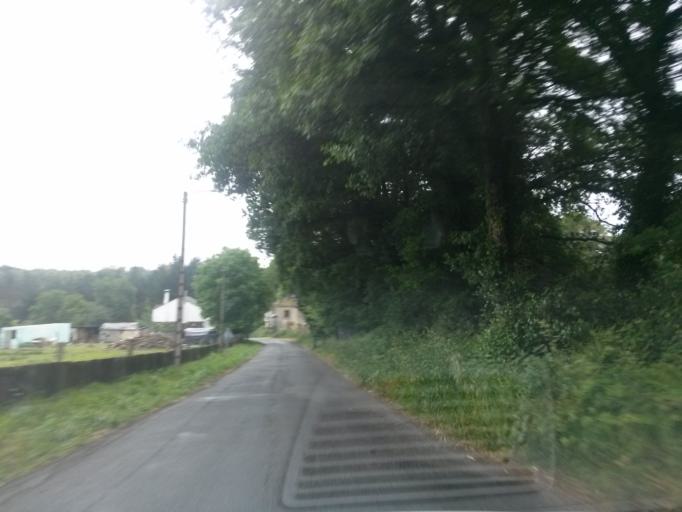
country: ES
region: Galicia
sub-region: Provincia de Lugo
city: Begonte
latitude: 43.1467
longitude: -7.6928
